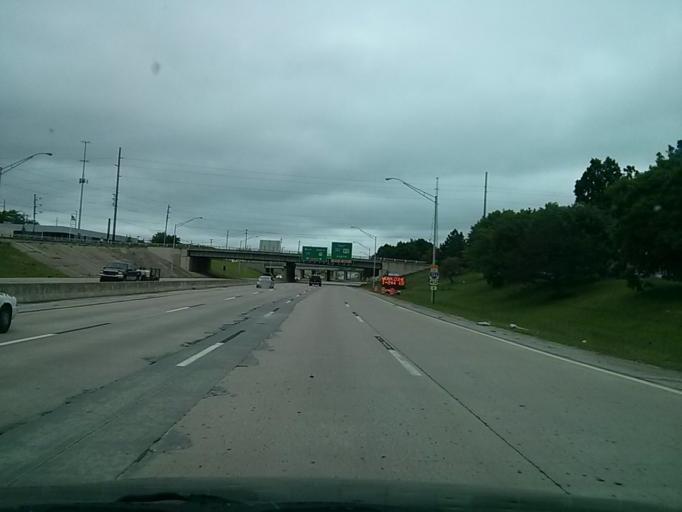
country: US
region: Oklahoma
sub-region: Tulsa County
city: Tulsa
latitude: 36.1542
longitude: -95.9802
